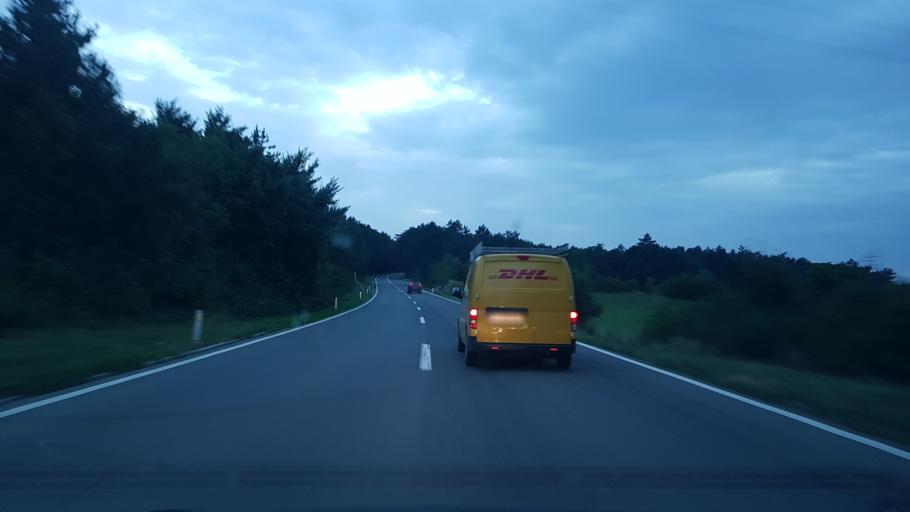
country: SI
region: Divaca
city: Divaca
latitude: 45.6913
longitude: 13.9819
